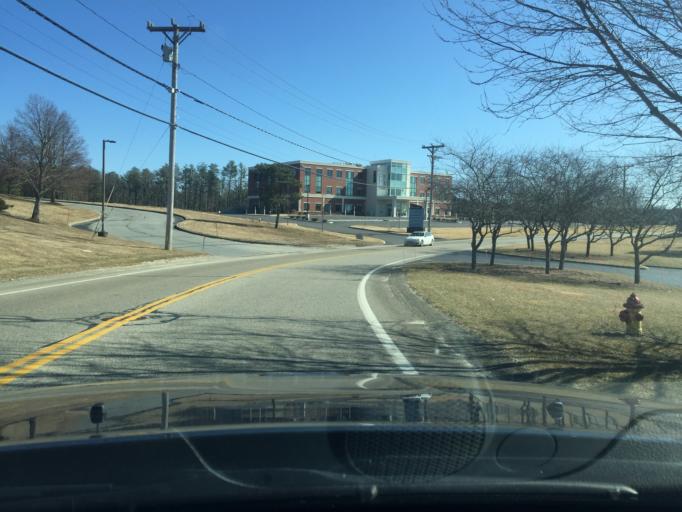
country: US
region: Massachusetts
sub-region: Plymouth County
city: North Plymouth
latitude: 41.9521
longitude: -70.7094
